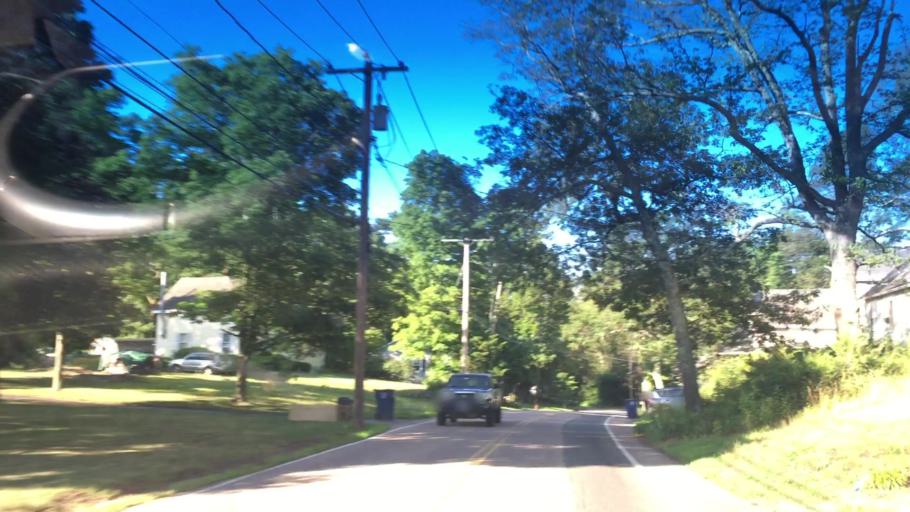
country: US
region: Massachusetts
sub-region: Norfolk County
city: Medway
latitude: 42.1433
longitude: -71.3923
